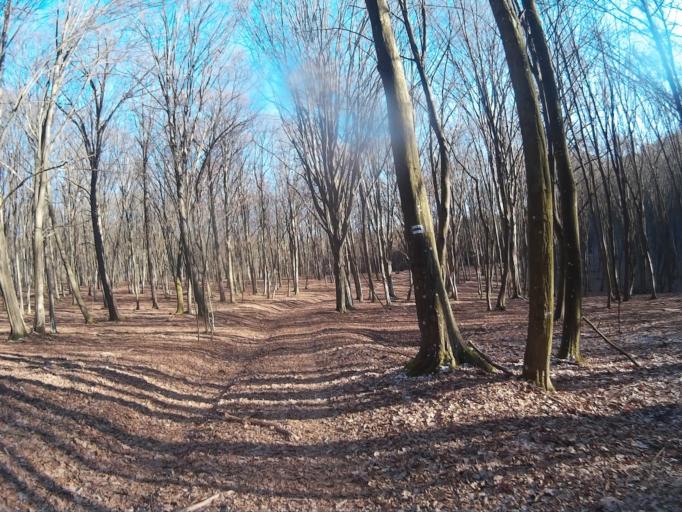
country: HU
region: Borsod-Abauj-Zemplen
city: Rudabanya
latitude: 48.4988
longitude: 20.5897
